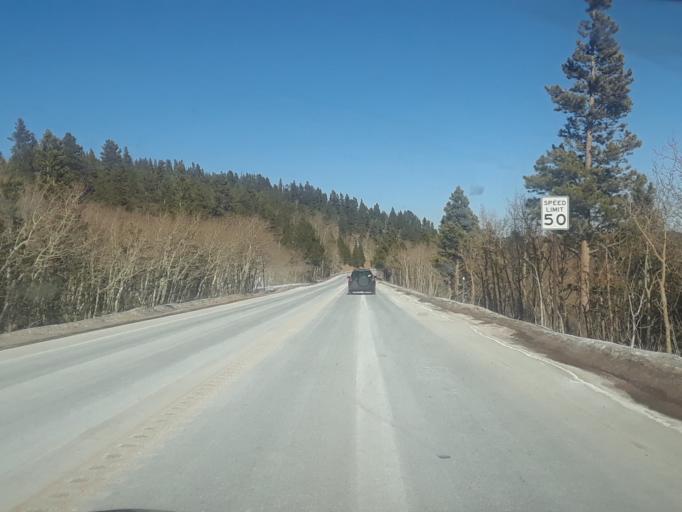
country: US
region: Colorado
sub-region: Boulder County
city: Nederland
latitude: 40.0905
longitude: -105.4955
